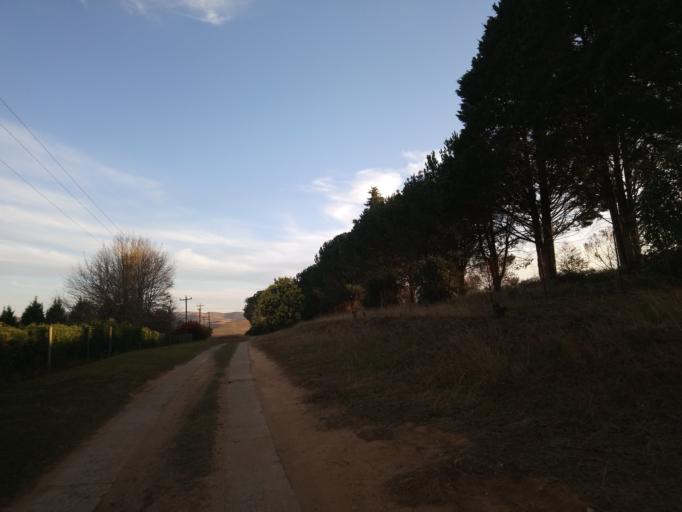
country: ZA
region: KwaZulu-Natal
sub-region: uMgungundlovu District Municipality
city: Mooirivier
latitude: -29.3290
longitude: 29.9203
